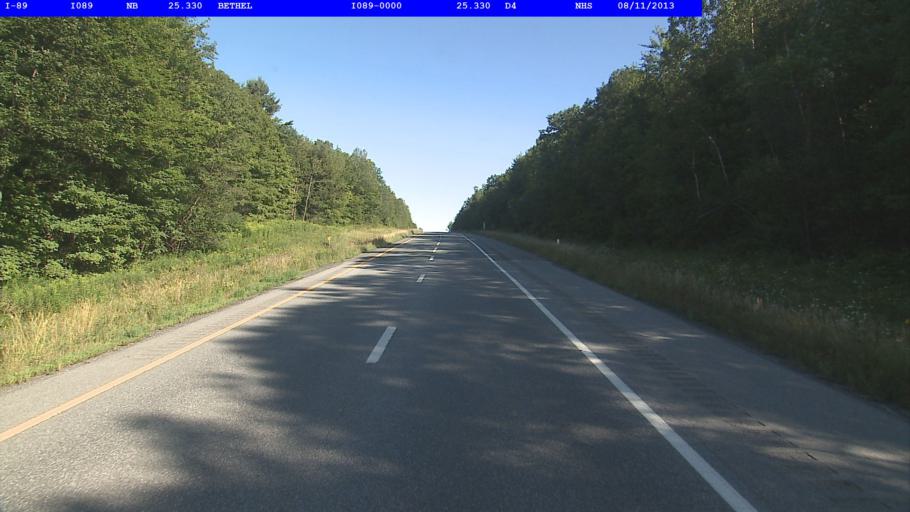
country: US
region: Vermont
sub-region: Orange County
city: Randolph
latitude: 43.8661
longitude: -72.6084
